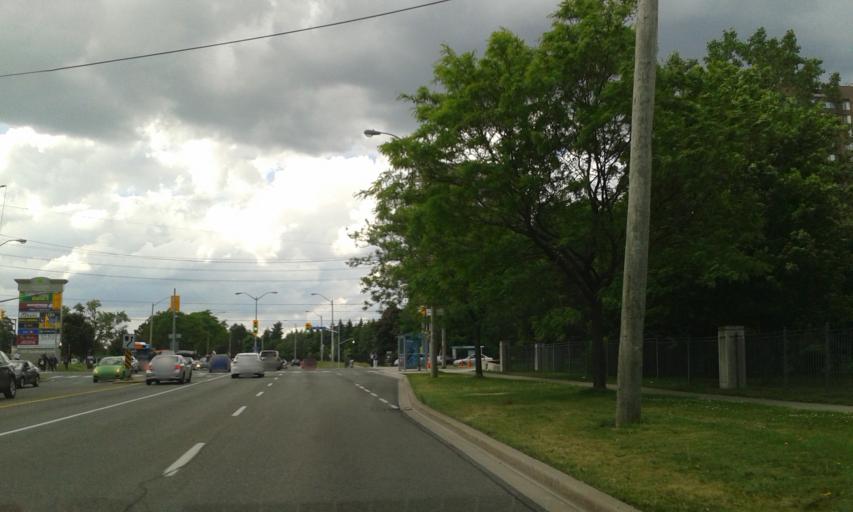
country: CA
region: Ontario
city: Scarborough
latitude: 43.8071
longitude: -79.2660
